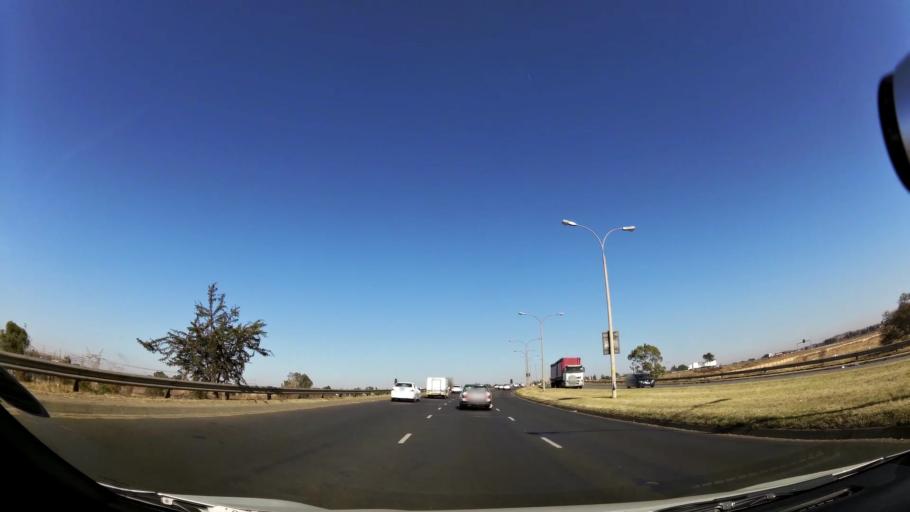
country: ZA
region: Gauteng
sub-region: Ekurhuleni Metropolitan Municipality
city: Germiston
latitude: -26.3048
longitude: 28.1147
